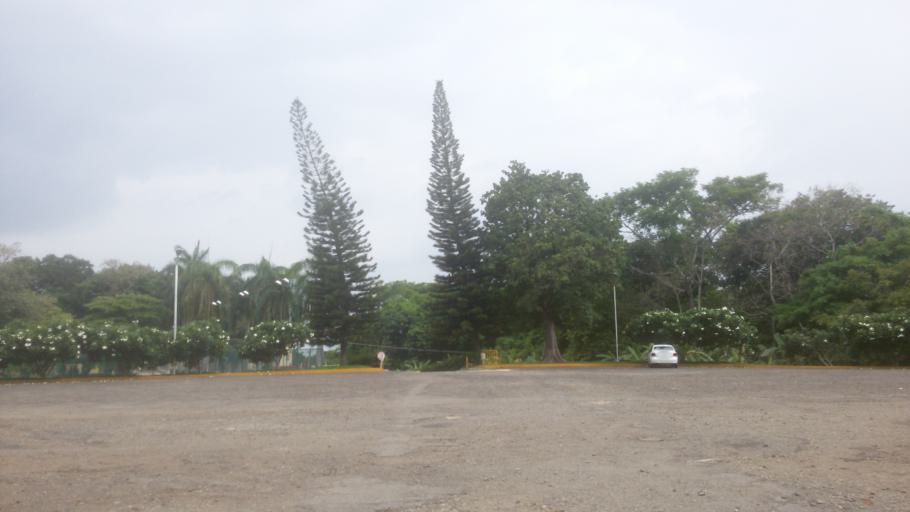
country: MX
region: Chiapas
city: Tapachula
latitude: 14.9206
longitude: -92.2742
